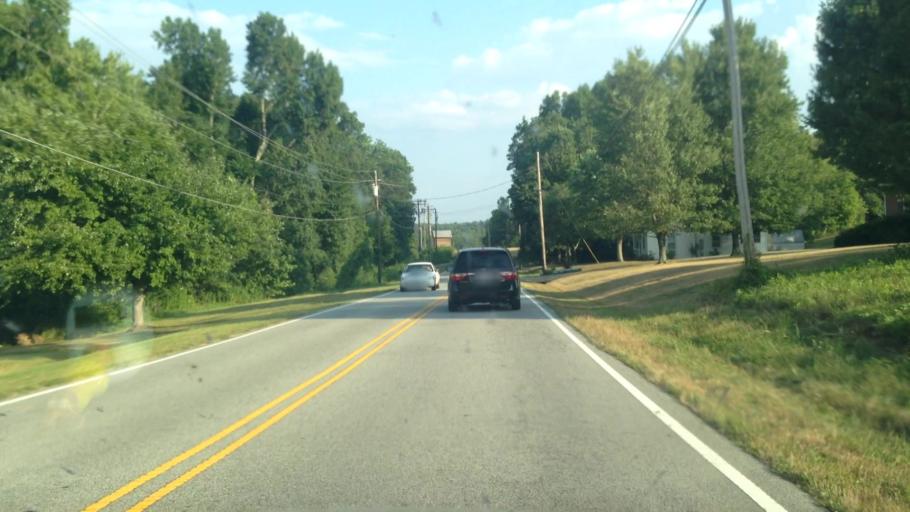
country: US
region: North Carolina
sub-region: Guilford County
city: High Point
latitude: 35.9571
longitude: -80.0731
